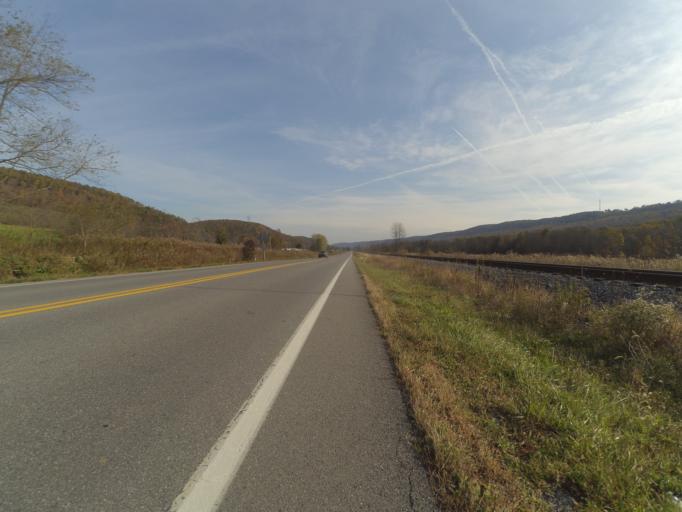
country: US
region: Pennsylvania
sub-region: Centre County
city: Stormstown
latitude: 40.8398
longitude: -77.9942
